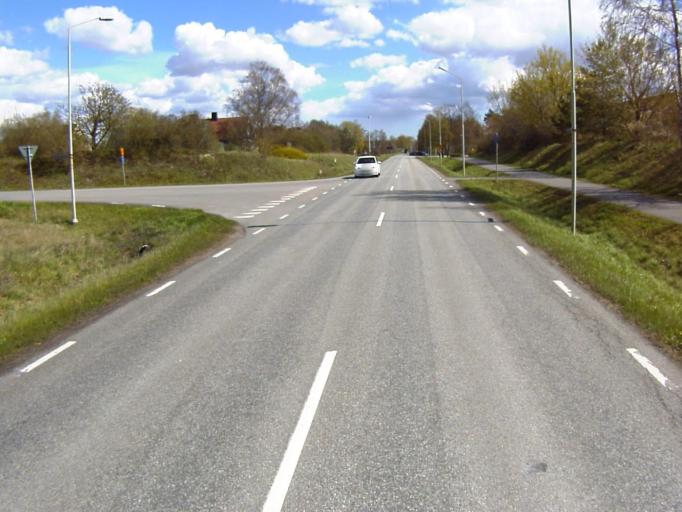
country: SE
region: Skane
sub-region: Kristianstads Kommun
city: Kristianstad
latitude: 56.0165
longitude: 14.1035
